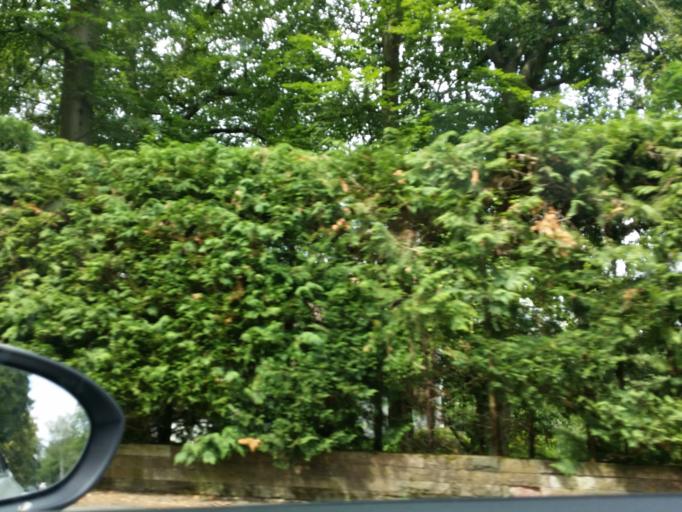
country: DE
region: Hesse
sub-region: Regierungsbezirk Darmstadt
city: Darmstadt
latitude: 49.8378
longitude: 8.6494
